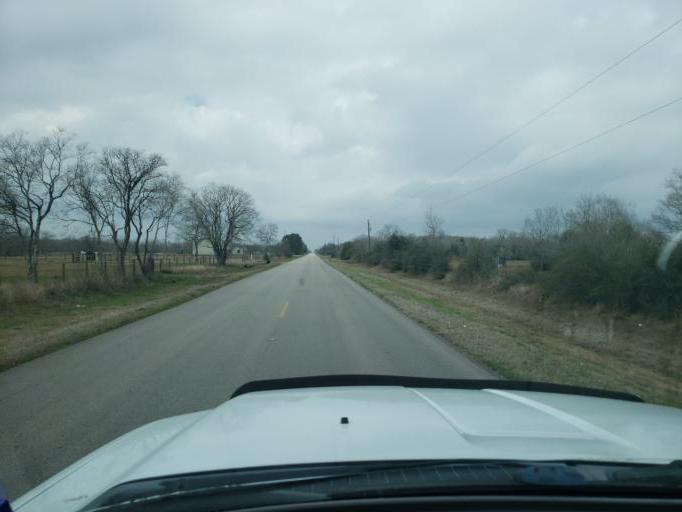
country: US
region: Texas
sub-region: Fort Bend County
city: Needville
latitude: 29.3745
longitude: -95.7356
